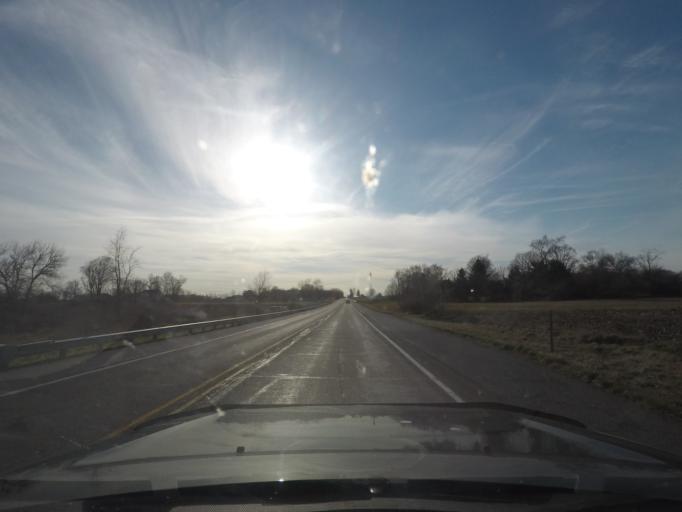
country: US
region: Indiana
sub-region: Saint Joseph County
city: North Liberty
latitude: 41.4488
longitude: -86.3526
